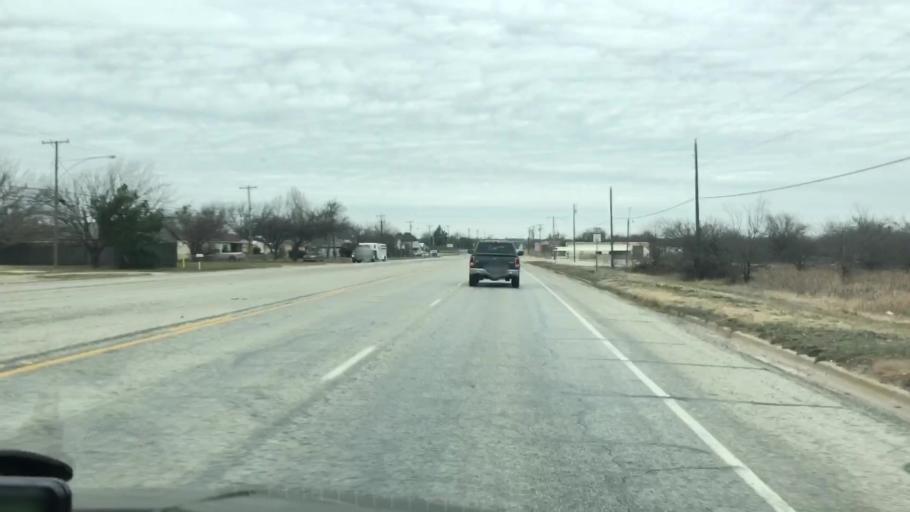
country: US
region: Texas
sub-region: Jack County
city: Jacksboro
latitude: 33.2046
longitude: -98.1525
